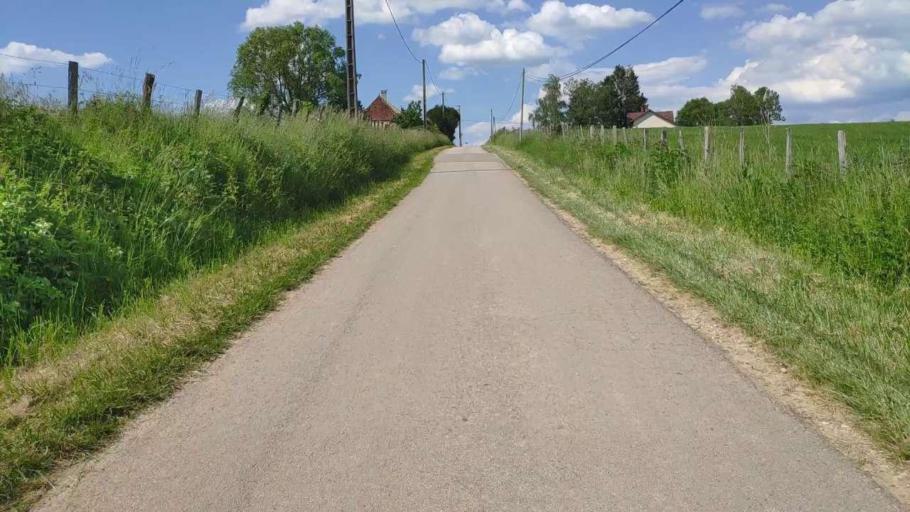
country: FR
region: Franche-Comte
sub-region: Departement du Jura
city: Bletterans
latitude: 46.8228
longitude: 5.4007
